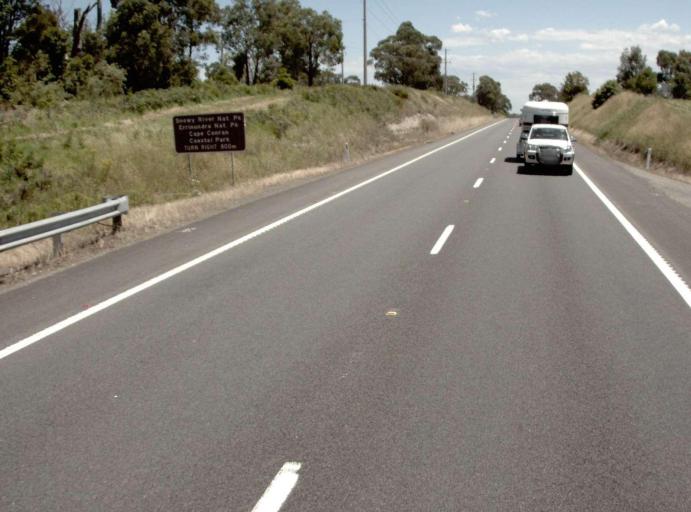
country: AU
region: Victoria
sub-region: East Gippsland
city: Lakes Entrance
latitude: -37.7026
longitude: 148.4778
